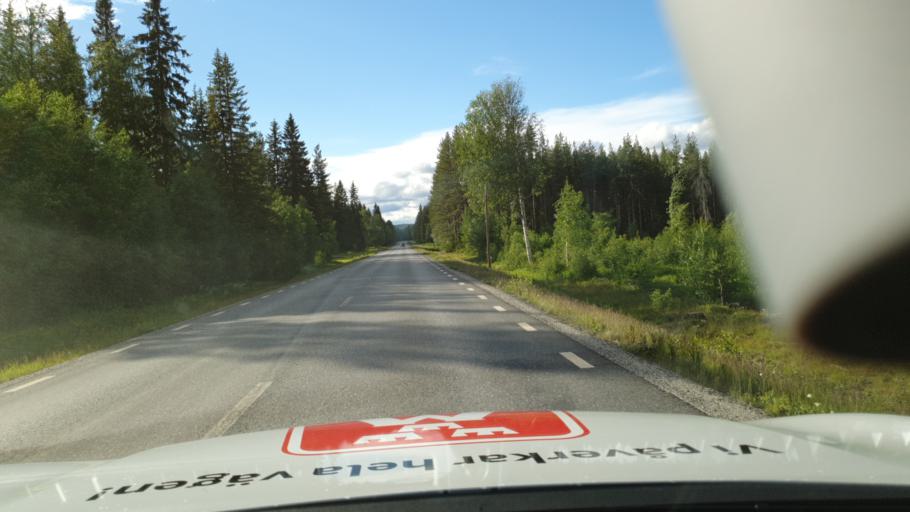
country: SE
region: Vaesterbotten
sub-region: Lycksele Kommun
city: Soderfors
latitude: 64.8063
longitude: 18.0843
